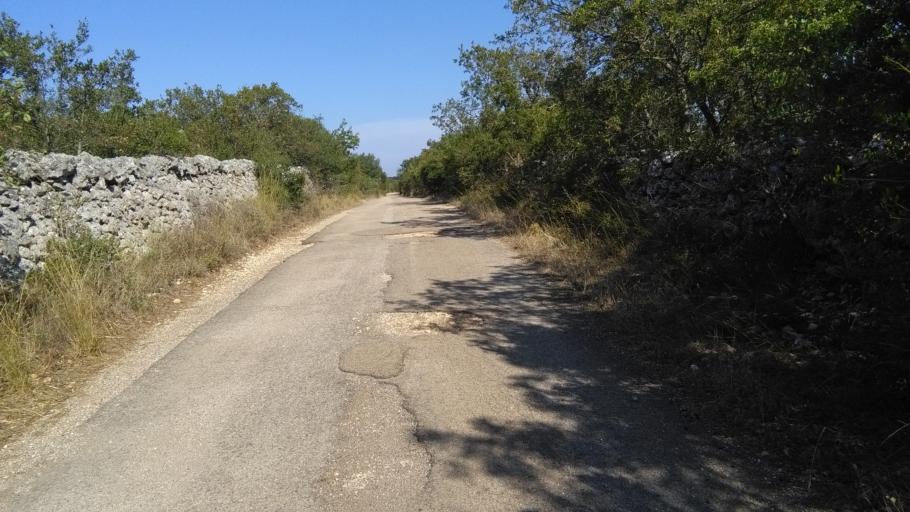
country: IT
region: Apulia
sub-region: Provincia di Bari
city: Putignano
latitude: 40.8205
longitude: 17.0382
